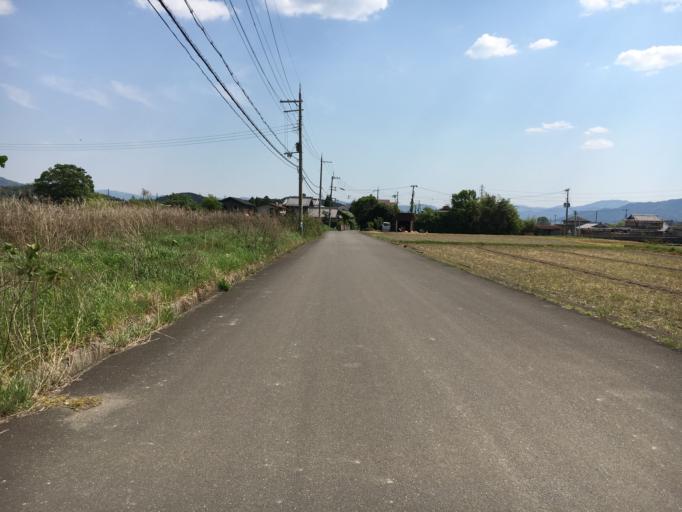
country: JP
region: Kyoto
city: Kameoka
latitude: 35.0808
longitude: 135.5561
